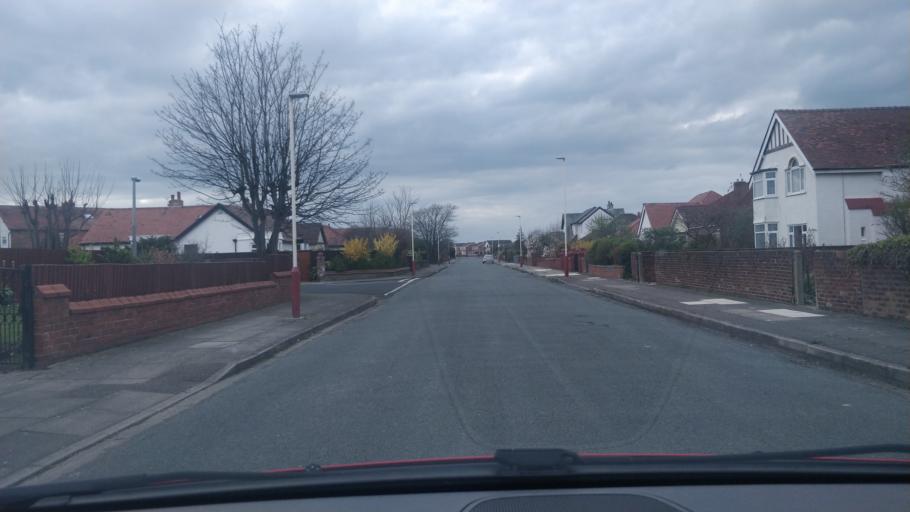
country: GB
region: England
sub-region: Sefton
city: Southport
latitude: 53.6063
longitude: -3.0415
